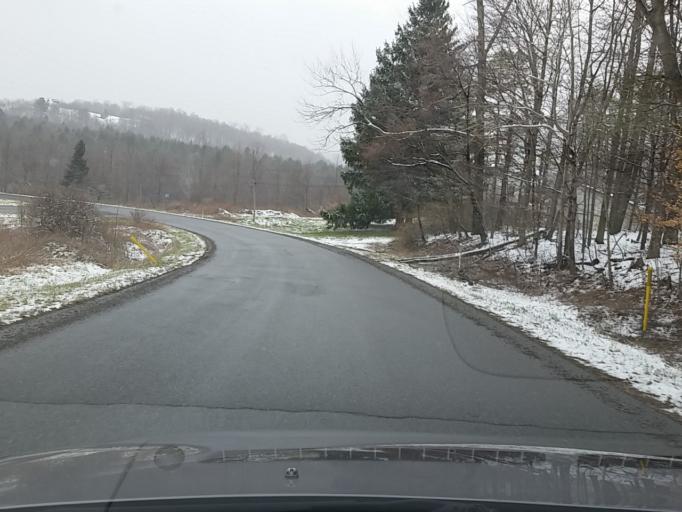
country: US
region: Pennsylvania
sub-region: Sullivan County
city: Laporte
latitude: 41.3785
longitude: -76.5198
